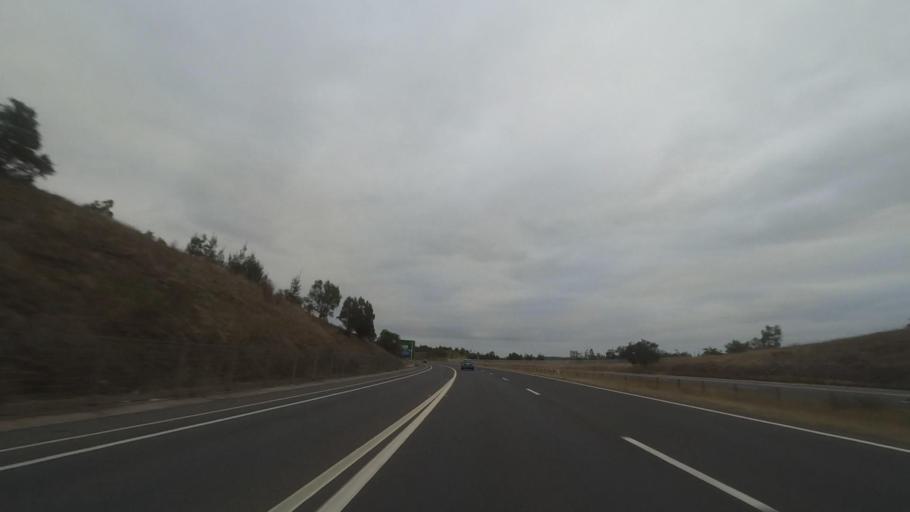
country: AU
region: New South Wales
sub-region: Shellharbour
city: Croom
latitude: -34.5882
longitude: 150.8445
